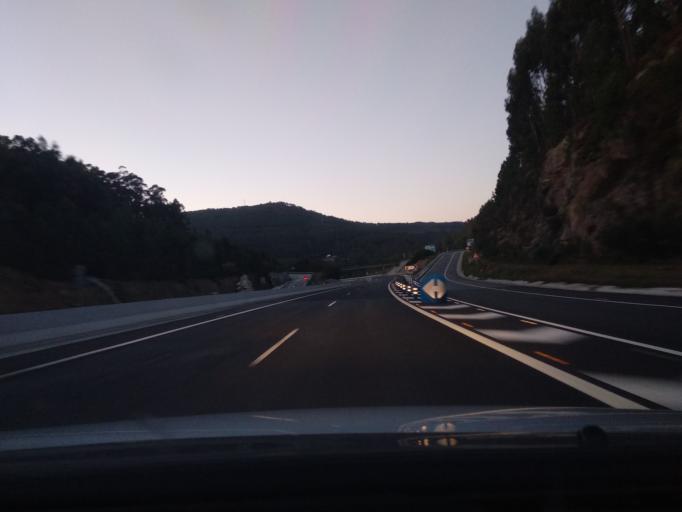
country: ES
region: Galicia
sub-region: Provincia de Pontevedra
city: Moana
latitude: 42.3022
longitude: -8.7196
